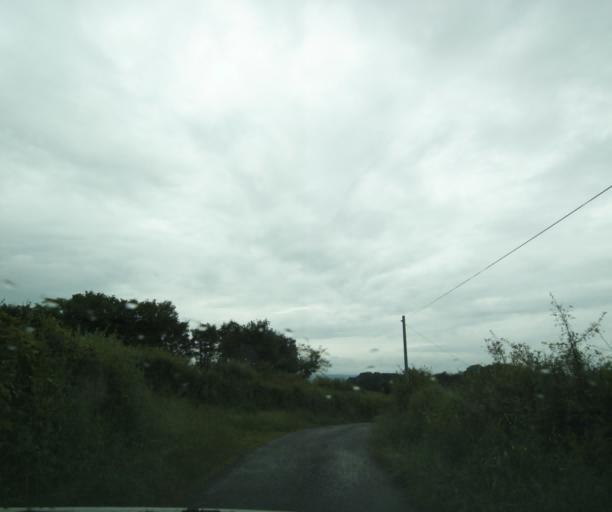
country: FR
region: Bourgogne
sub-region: Departement de Saone-et-Loire
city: Ciry-le-Noble
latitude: 46.5353
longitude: 4.2954
